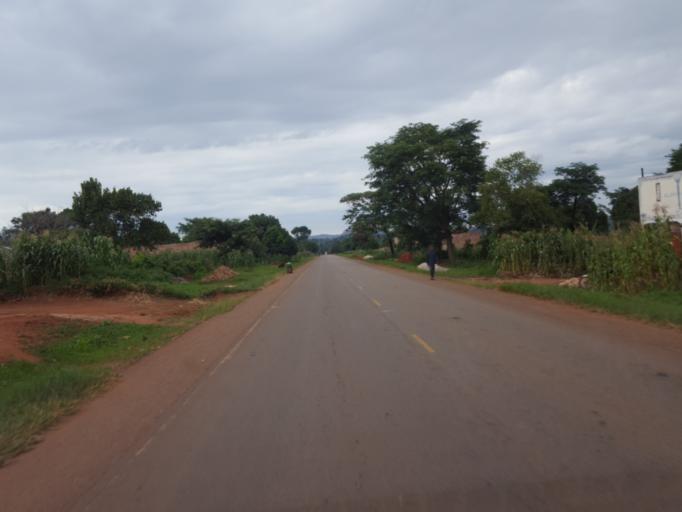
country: UG
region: Central Region
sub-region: Kiboga District
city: Kiboga
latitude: 1.0254
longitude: 31.6827
